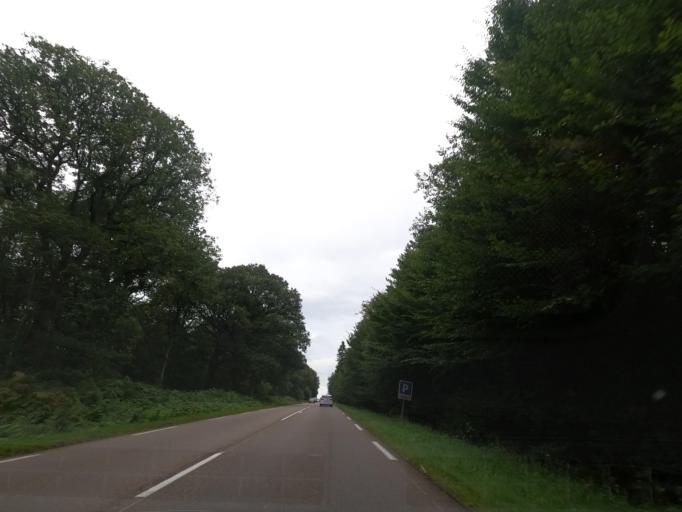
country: FR
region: Haute-Normandie
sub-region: Departement de l'Eure
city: Bourgtheroulde-Infreville
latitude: 49.2801
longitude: 0.8329
